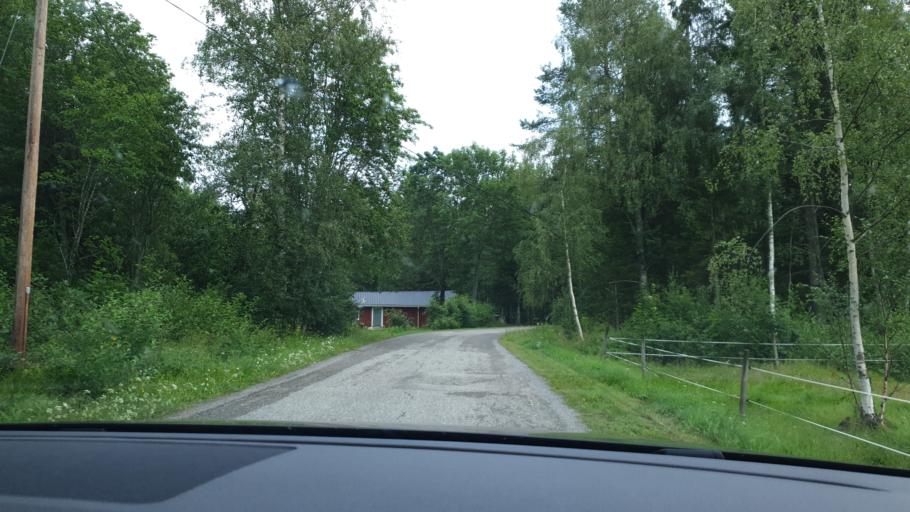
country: SE
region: Gaevleborg
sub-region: Hudiksvalls Kommun
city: Iggesund
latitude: 61.5378
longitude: 17.0097
